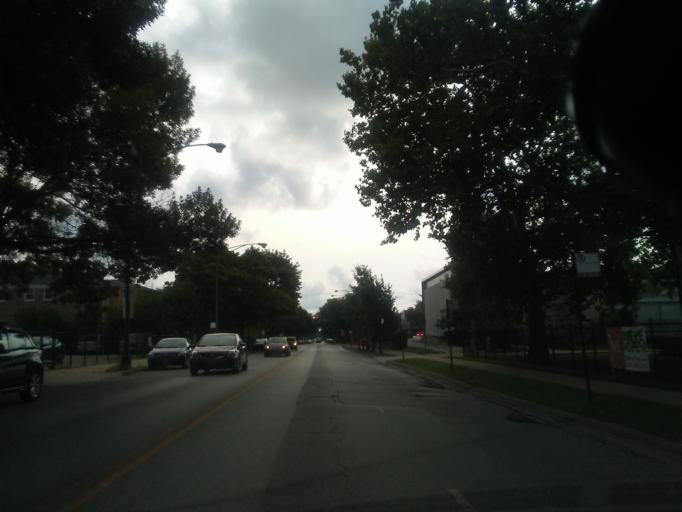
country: US
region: Illinois
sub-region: Cook County
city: Lincolnwood
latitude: 42.0119
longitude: -87.7061
